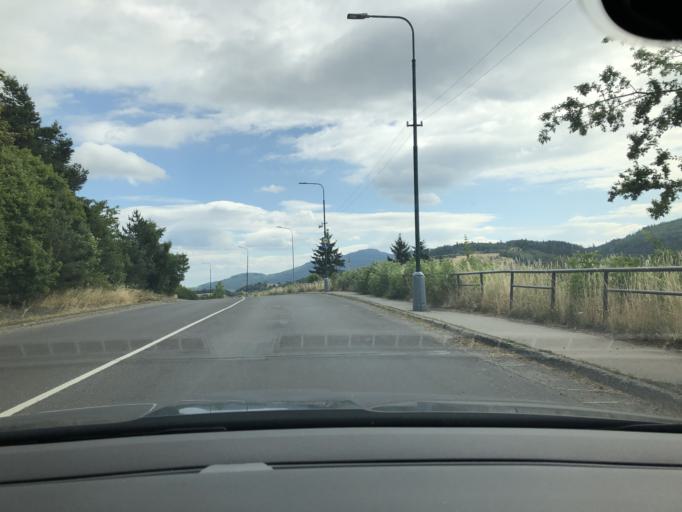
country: SK
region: Banskobystricky
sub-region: Okres Banska Bystrica
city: Banska Stiavnica
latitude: 48.4609
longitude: 18.9055
